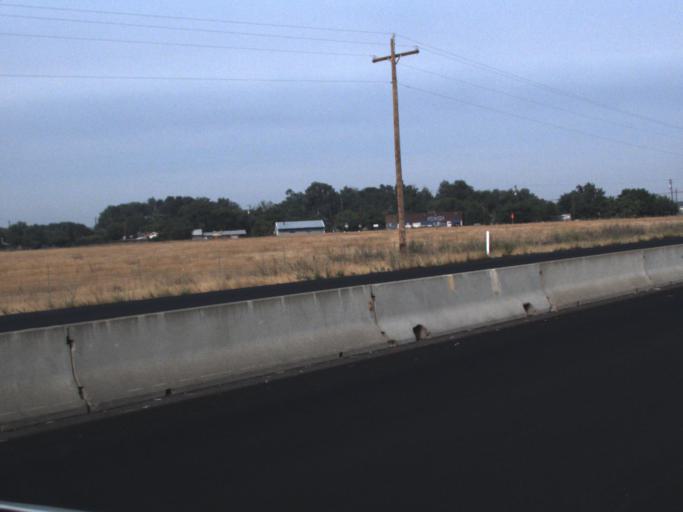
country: US
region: Washington
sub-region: Yakima County
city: Wapato
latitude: 46.4302
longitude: -120.4141
